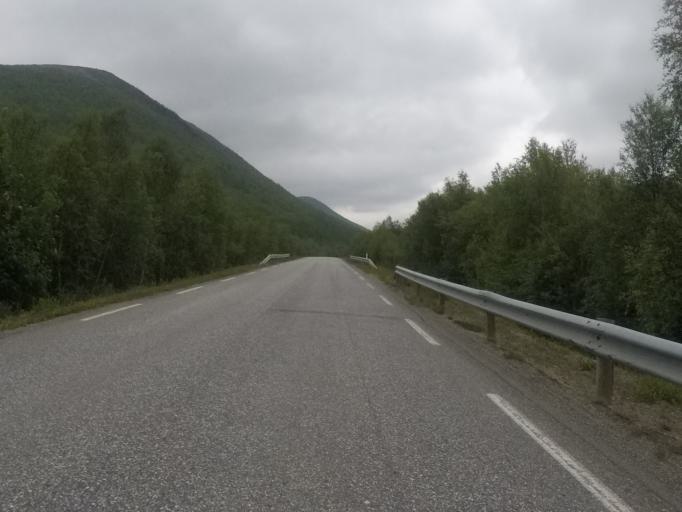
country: FI
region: Lapland
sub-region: Pohjois-Lappi
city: Utsjoki
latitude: 69.8199
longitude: 26.2483
